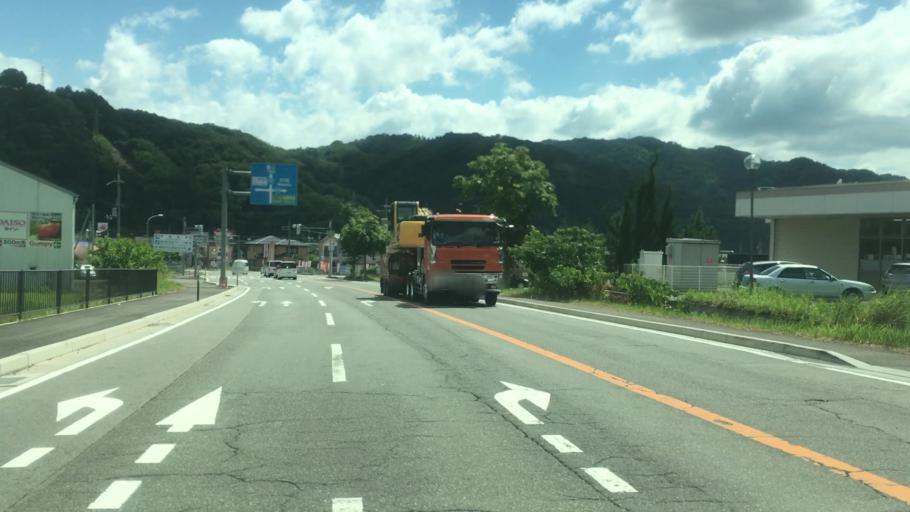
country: JP
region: Hyogo
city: Toyooka
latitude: 35.4706
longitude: 134.7689
